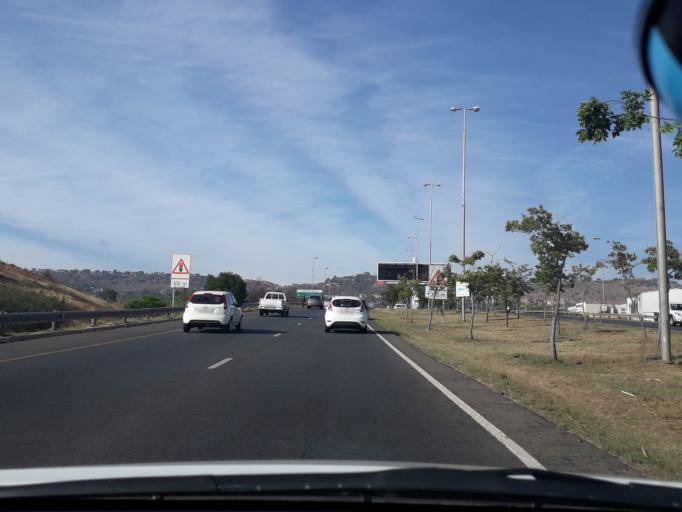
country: ZA
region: Gauteng
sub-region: City of Johannesburg Metropolitan Municipality
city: Roodepoort
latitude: -26.1236
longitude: 27.9108
